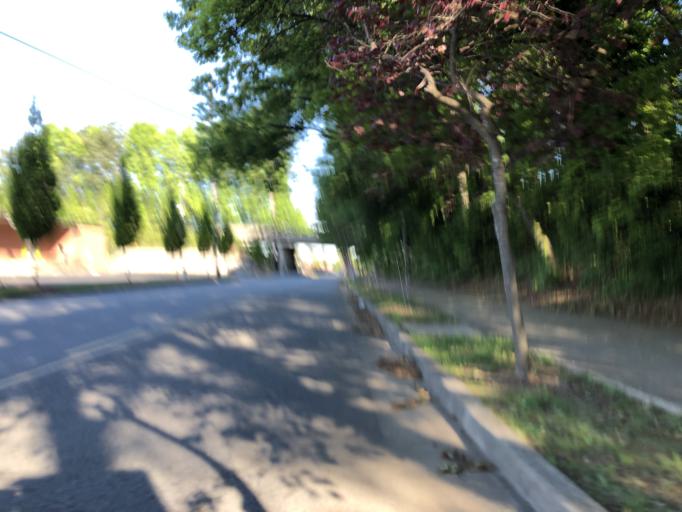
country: US
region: Georgia
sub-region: Fulton County
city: Atlanta
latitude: 33.7329
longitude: -84.4223
